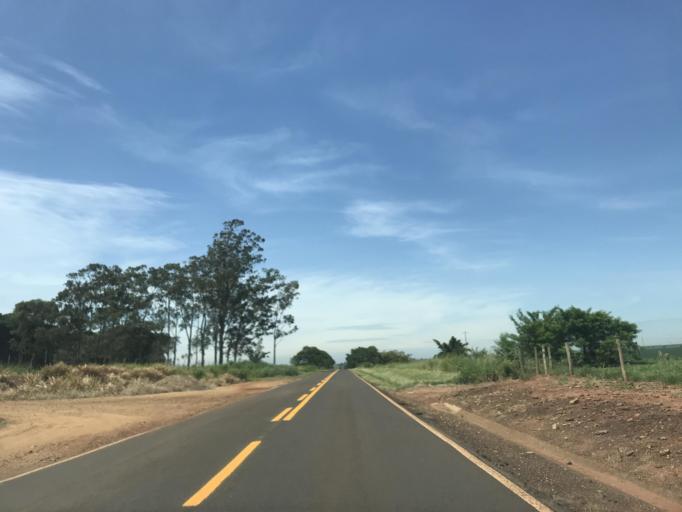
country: BR
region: Parana
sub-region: Terra Rica
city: Terra Rica
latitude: -22.7990
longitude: -52.6531
